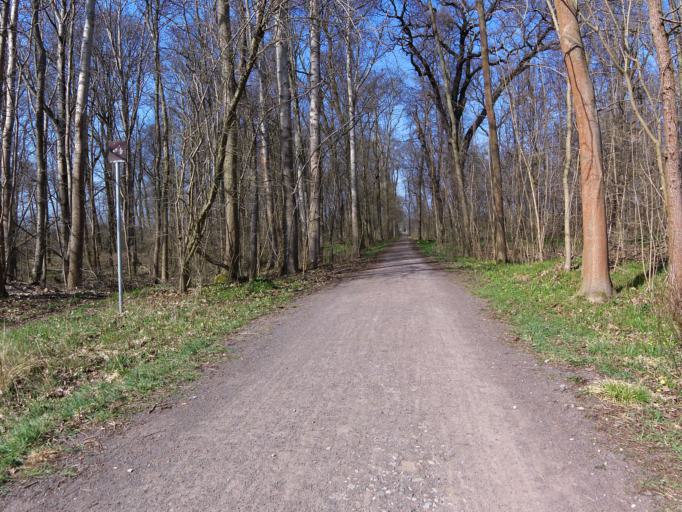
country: DE
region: Saxony
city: Leipzig
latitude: 51.3690
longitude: 12.2978
